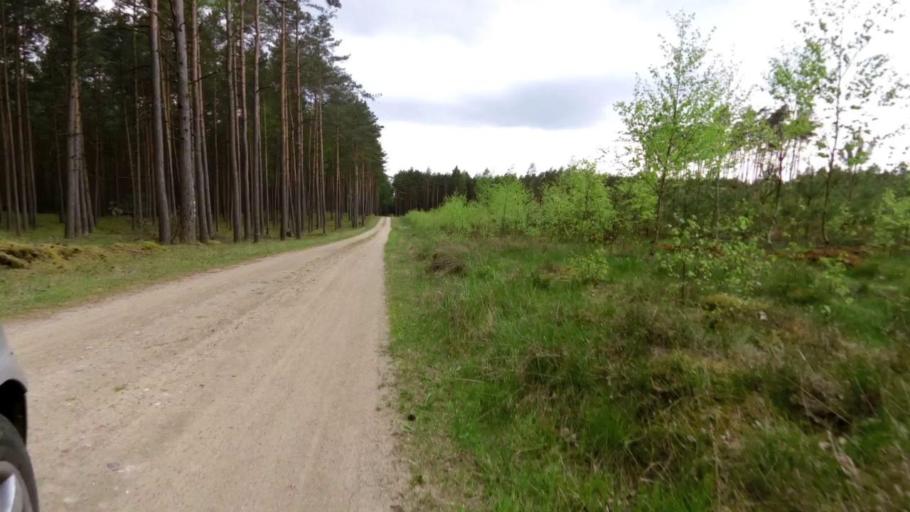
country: PL
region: West Pomeranian Voivodeship
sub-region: Powiat walecki
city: Walcz
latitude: 53.2718
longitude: 16.3509
